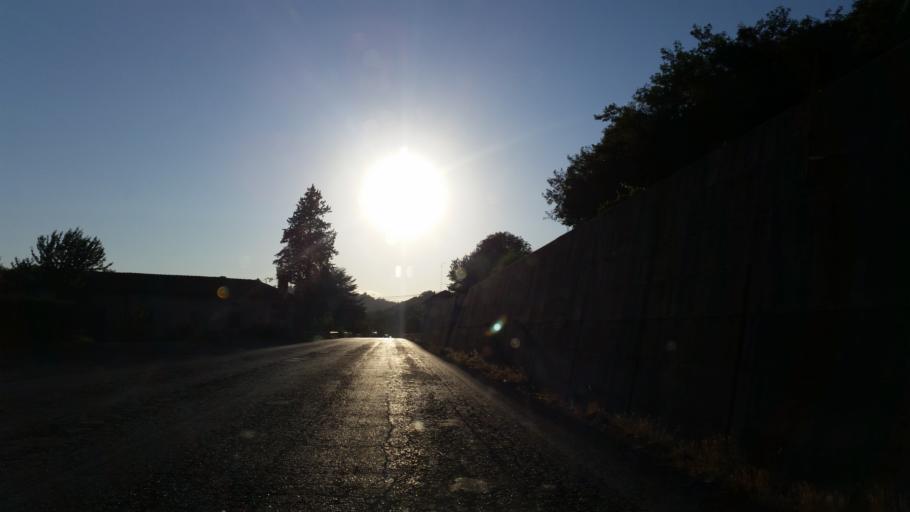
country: IT
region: Piedmont
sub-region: Provincia di Cuneo
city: Santo Stefano Belbo
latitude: 44.7128
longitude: 8.2616
